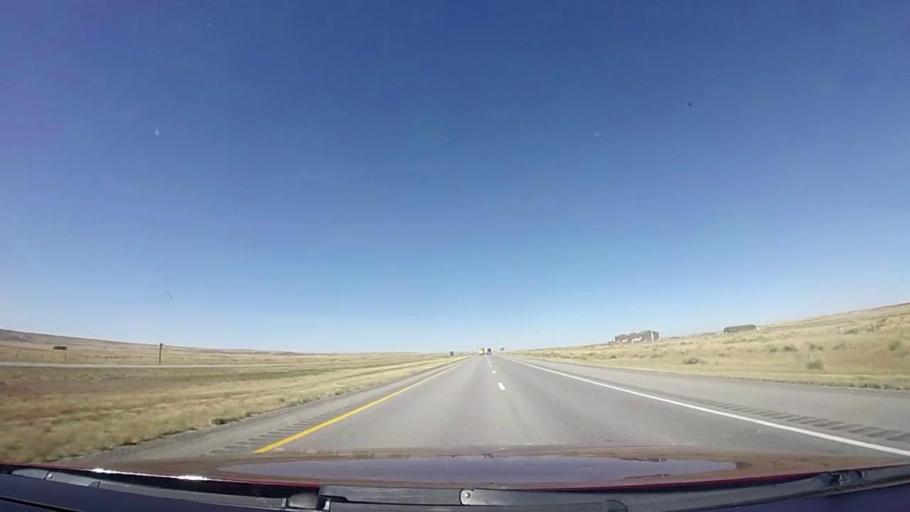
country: US
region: Wyoming
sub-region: Carbon County
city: Rawlins
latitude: 41.6675
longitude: -108.0179
